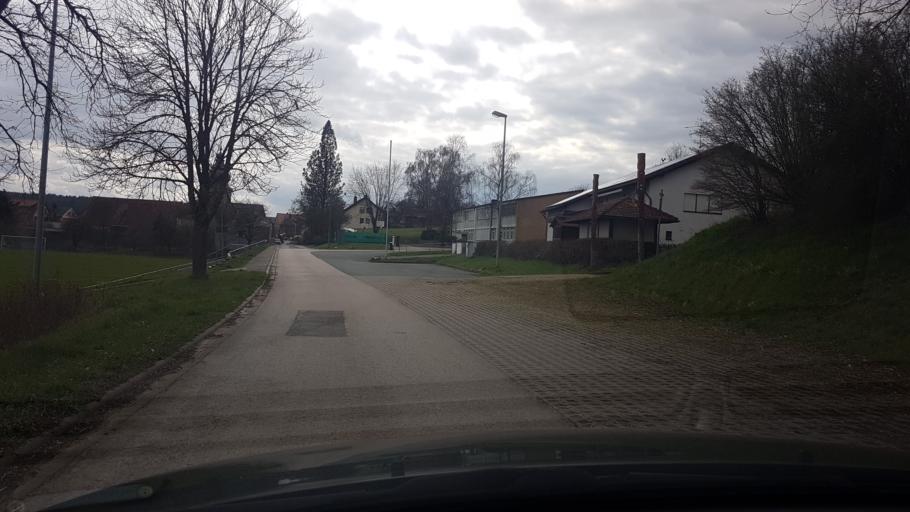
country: DE
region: Bavaria
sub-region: Upper Franconia
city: Pettstadt
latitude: 49.8031
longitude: 10.9263
